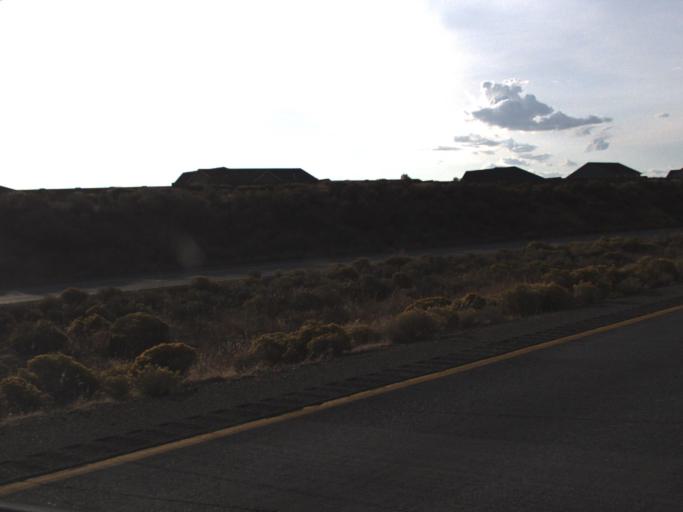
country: US
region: Washington
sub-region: Benton County
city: Richland
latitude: 46.2059
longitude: -119.3366
